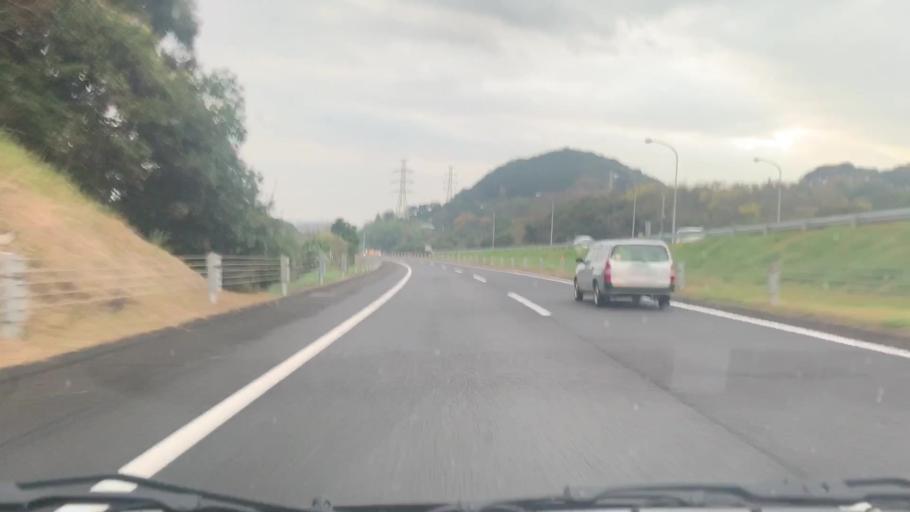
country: JP
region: Nagasaki
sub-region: Isahaya-shi
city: Isahaya
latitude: 32.8608
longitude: 130.0023
